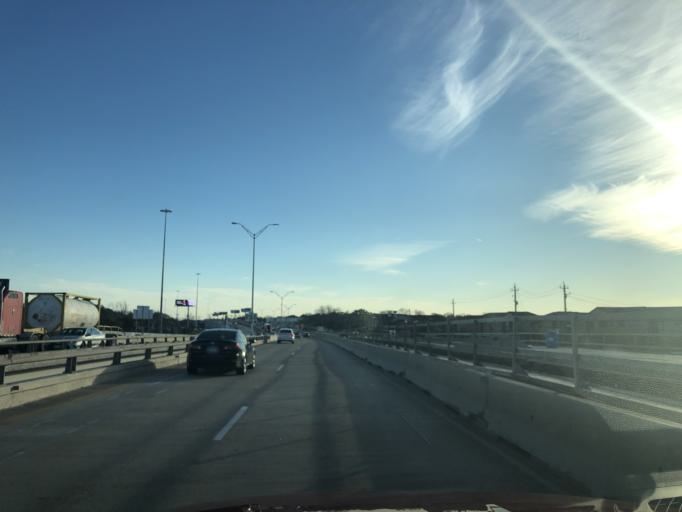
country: US
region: Texas
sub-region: Harris County
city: Deer Park
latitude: 29.6820
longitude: -95.1554
